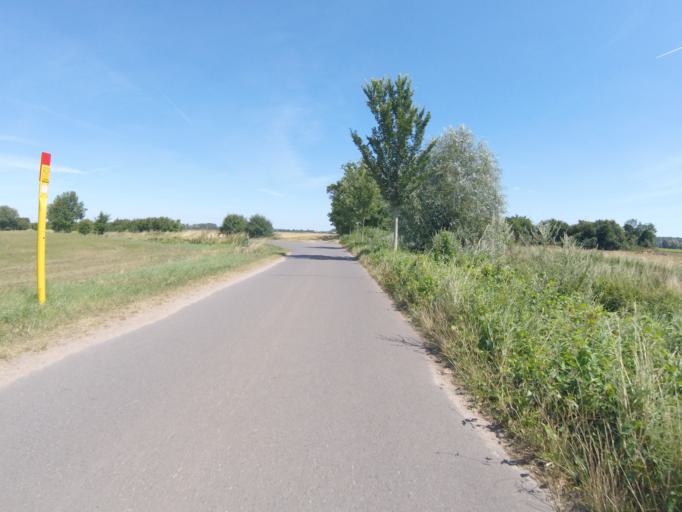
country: DE
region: Brandenburg
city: Mittenwalde
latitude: 52.2763
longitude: 13.5415
